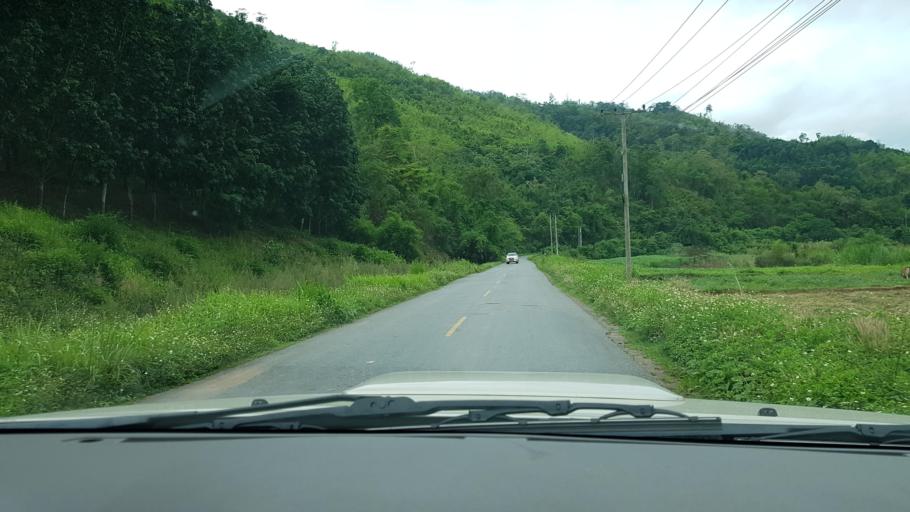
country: LA
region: Loungnamtha
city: Muang Nale
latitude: 20.3737
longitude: 101.7244
